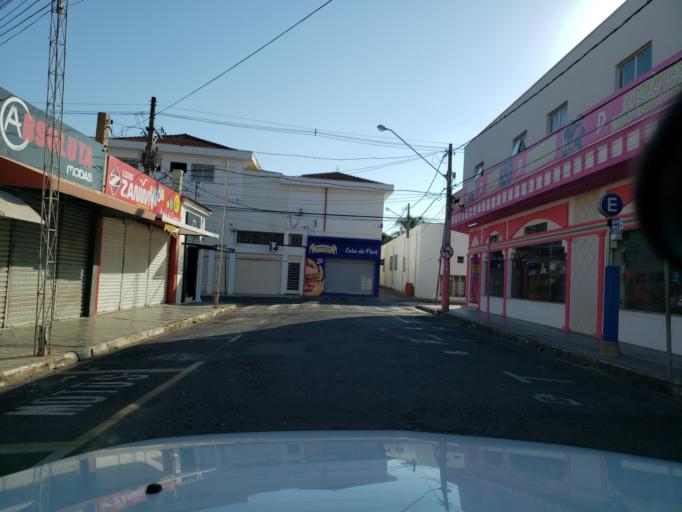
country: BR
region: Sao Paulo
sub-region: Moji-Guacu
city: Mogi-Gaucu
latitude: -22.3724
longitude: -46.9413
